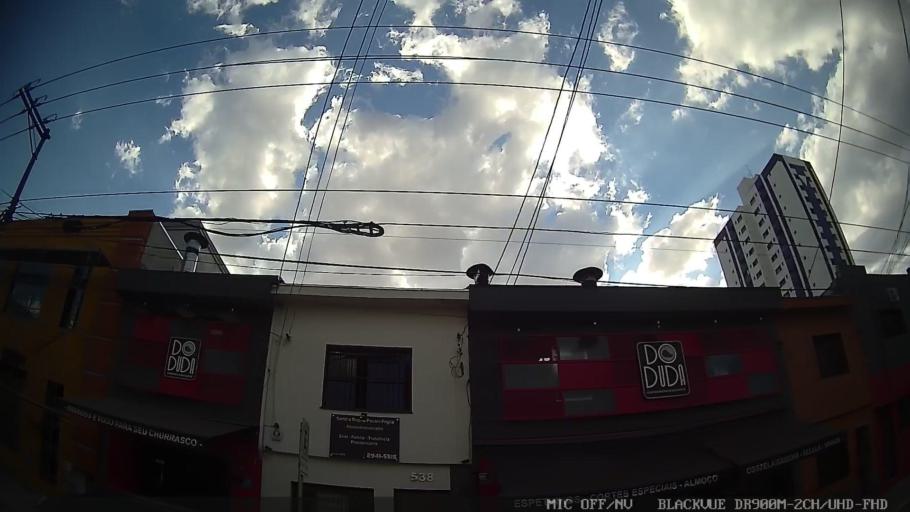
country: BR
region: Sao Paulo
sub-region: Sao Paulo
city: Sao Paulo
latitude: -23.5439
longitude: -46.5693
